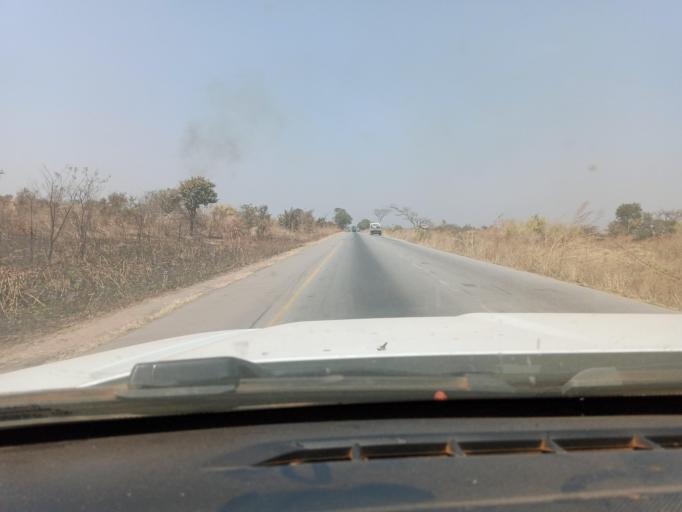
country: ZM
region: Copperbelt
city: Luanshya
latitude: -12.9989
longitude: 28.4226
